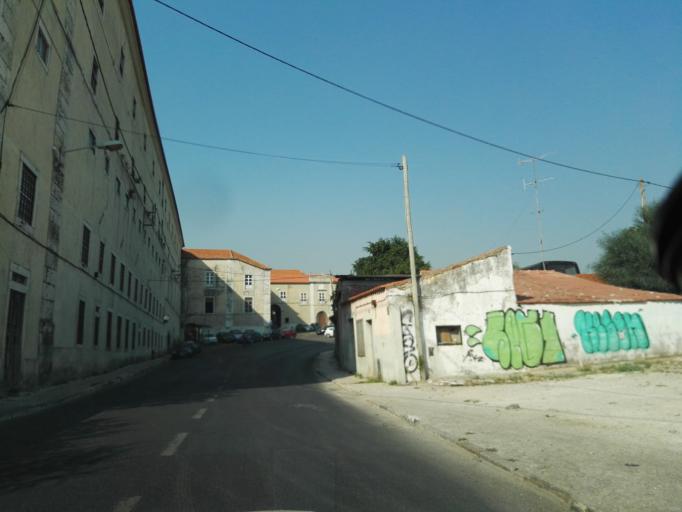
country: PT
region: Lisbon
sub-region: Lisbon
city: Lisbon
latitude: 38.7392
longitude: -9.1177
